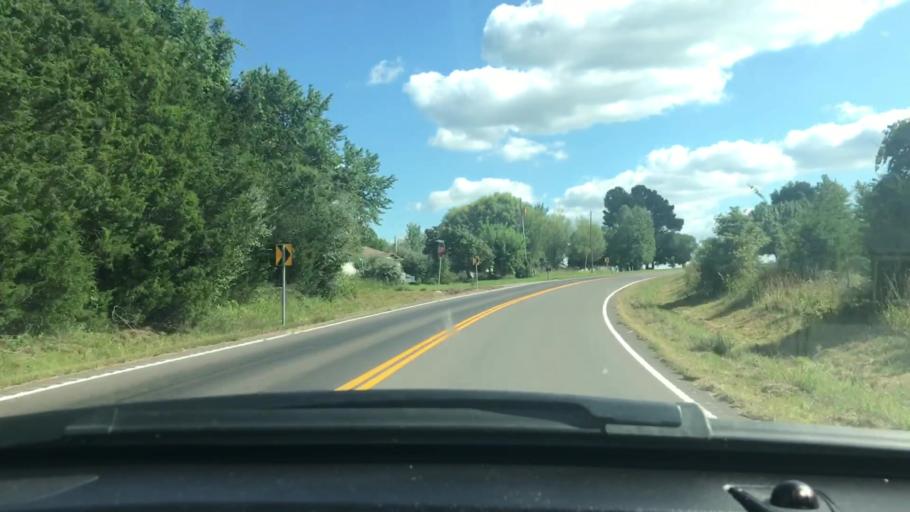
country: US
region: Missouri
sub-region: Wright County
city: Mountain Grove
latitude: 37.2528
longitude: -92.3005
